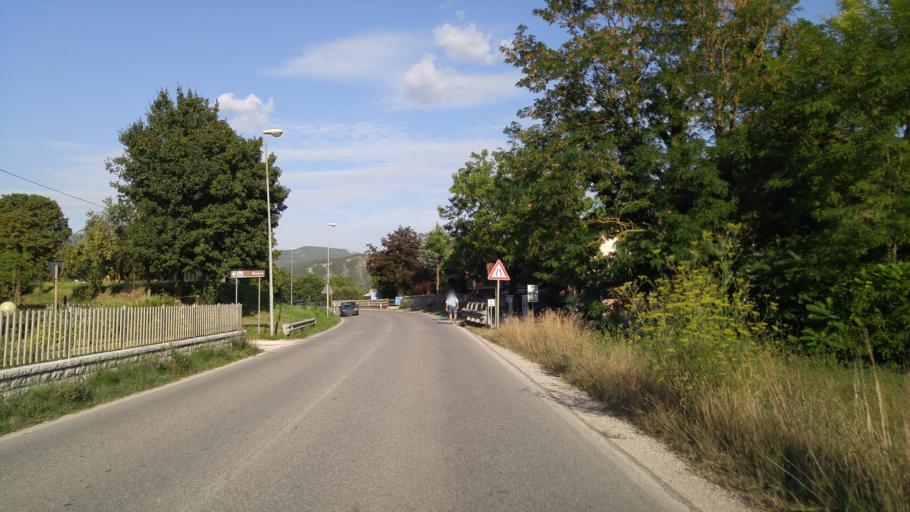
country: IT
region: The Marches
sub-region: Provincia di Pesaro e Urbino
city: Acqualagna
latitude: 43.6132
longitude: 12.6470
